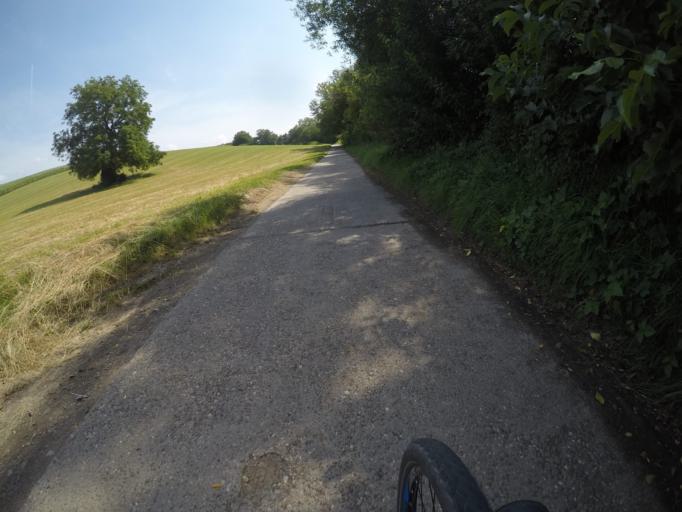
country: DE
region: Baden-Wuerttemberg
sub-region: Karlsruhe Region
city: Gondelsheim
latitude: 49.0538
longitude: 8.6667
